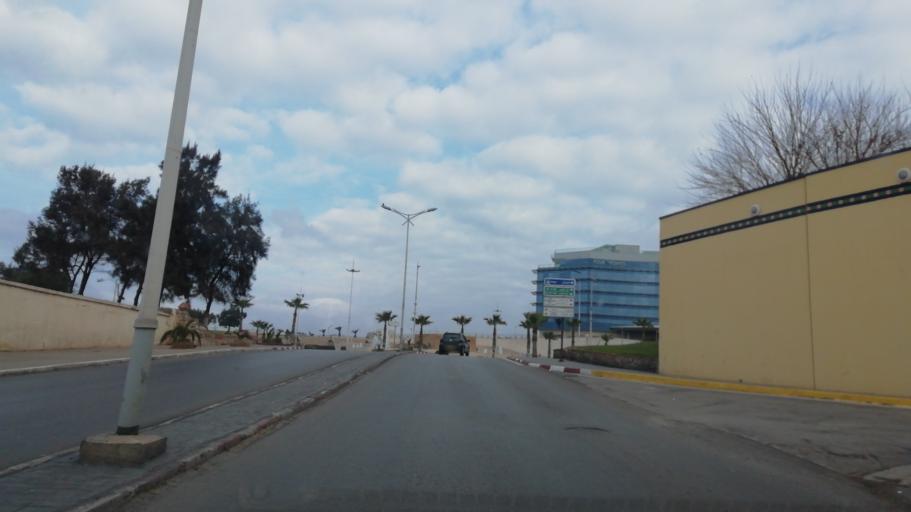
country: DZ
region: Oran
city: Oran
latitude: 35.7149
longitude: -0.6121
